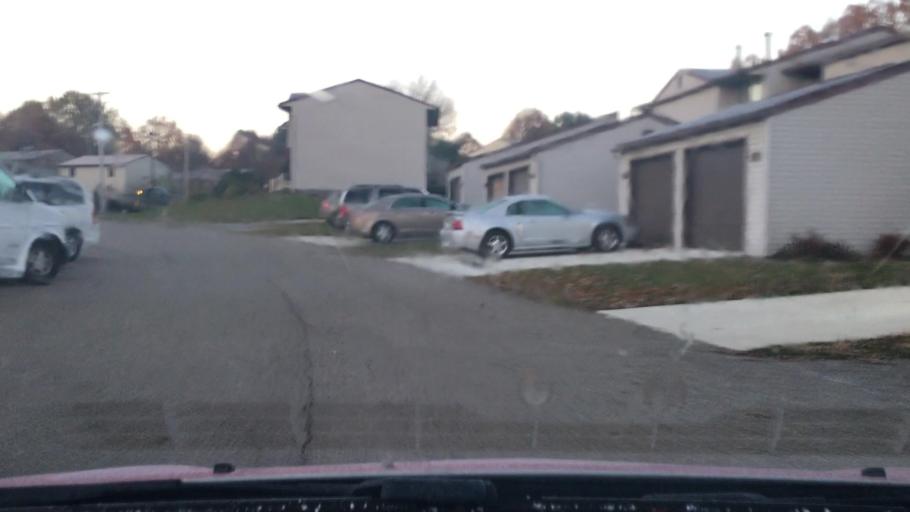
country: US
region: Ohio
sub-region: Wayne County
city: Wooster
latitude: 40.7883
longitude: -81.9275
